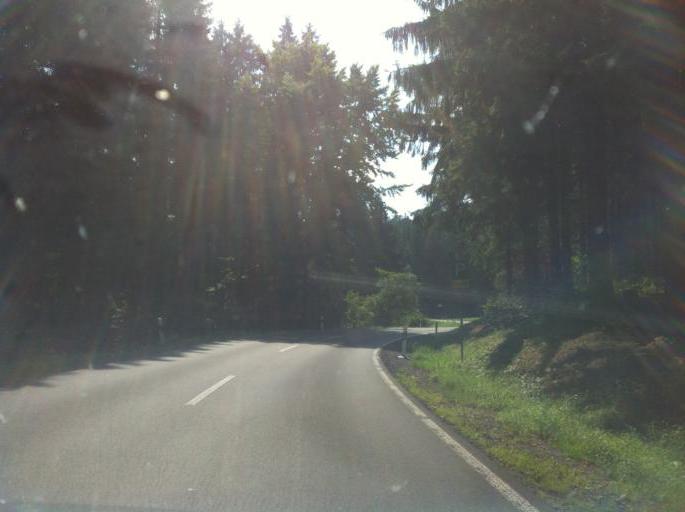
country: DE
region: Thuringia
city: Grossbreitenbach
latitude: 50.6002
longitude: 10.9843
